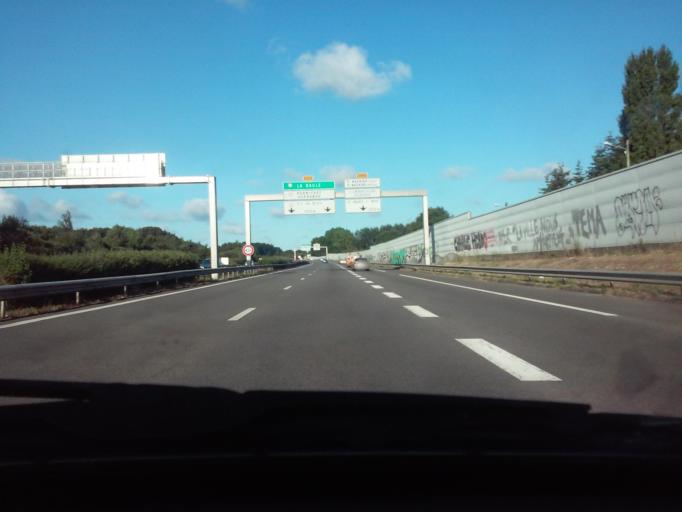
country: FR
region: Pays de la Loire
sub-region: Departement de la Loire-Atlantique
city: Saint-Nazaire
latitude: 47.2890
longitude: -2.2417
